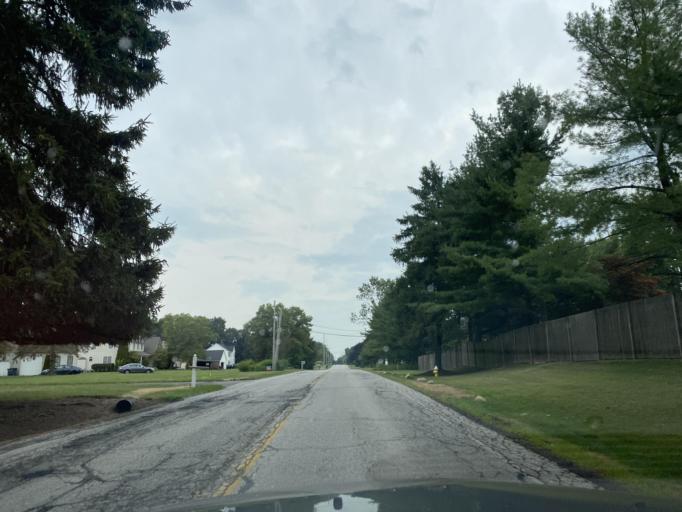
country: US
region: Ohio
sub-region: Summit County
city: Fairlawn
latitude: 41.1446
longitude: -81.5873
